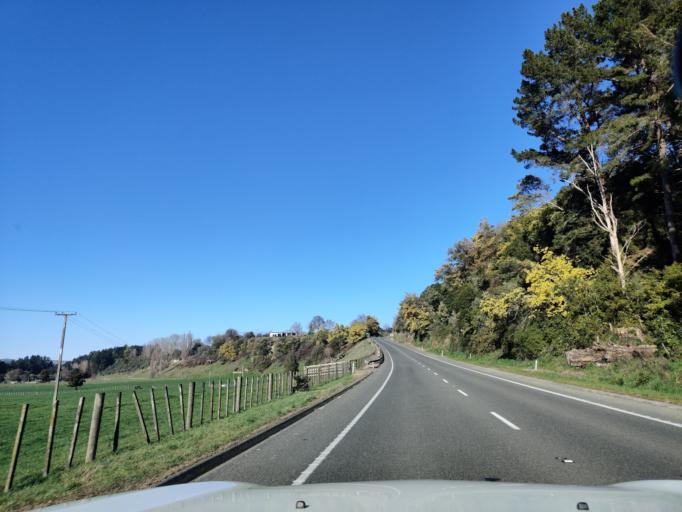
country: NZ
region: Manawatu-Wanganui
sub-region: Rangitikei District
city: Bulls
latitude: -39.9195
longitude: 175.6329
